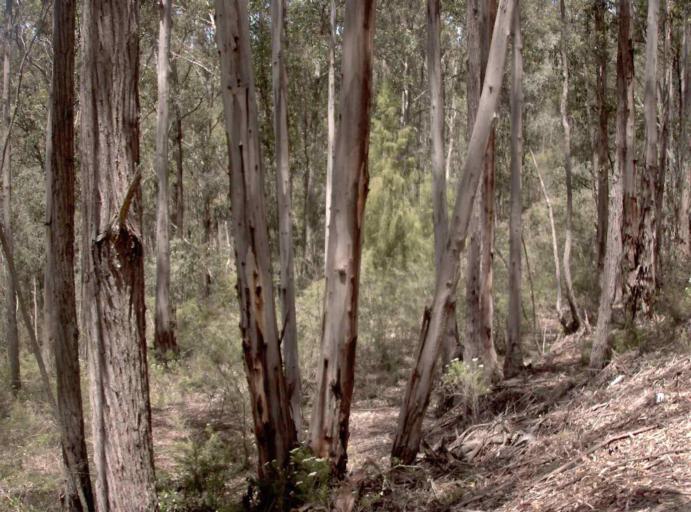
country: AU
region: Victoria
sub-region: East Gippsland
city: Lakes Entrance
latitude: -37.5992
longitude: 147.8888
